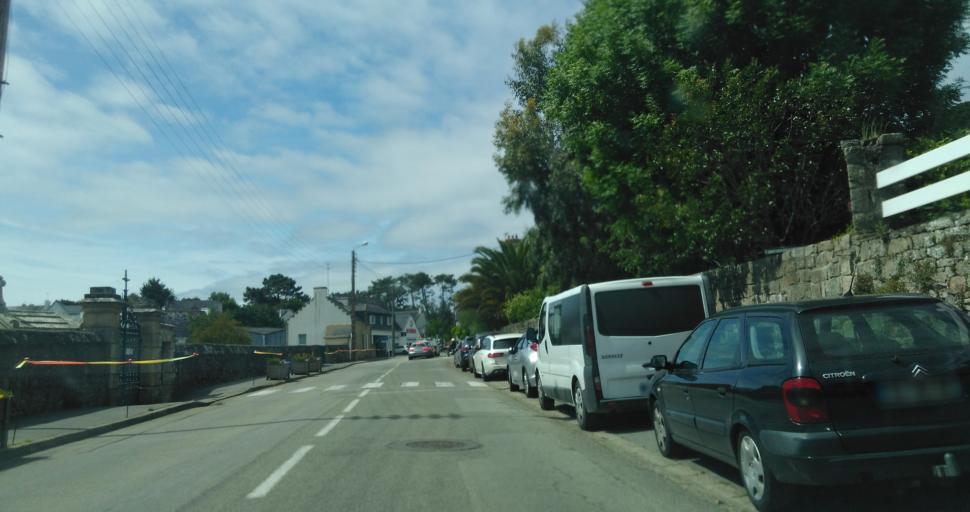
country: FR
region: Brittany
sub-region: Departement du Morbihan
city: La Trinite-sur-Mer
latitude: 47.5879
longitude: -3.0314
